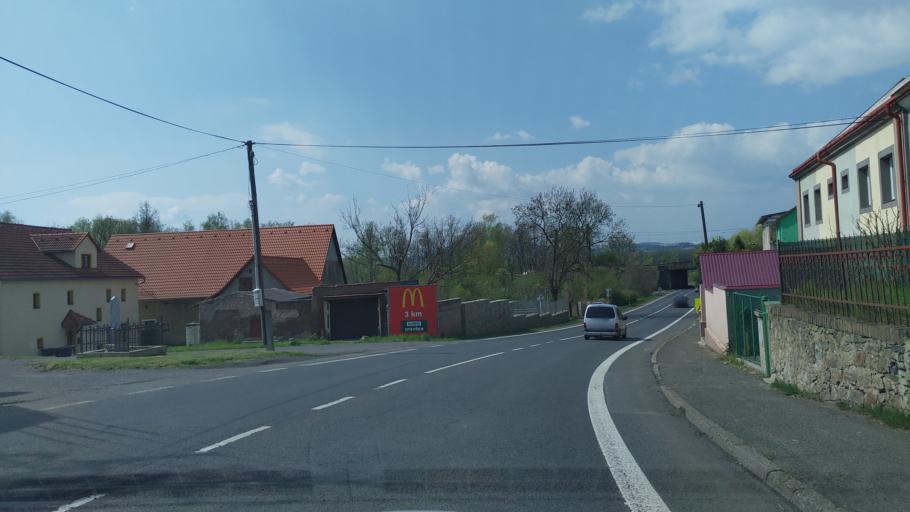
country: CZ
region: Ustecky
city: Krupka
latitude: 50.6719
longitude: 13.8940
